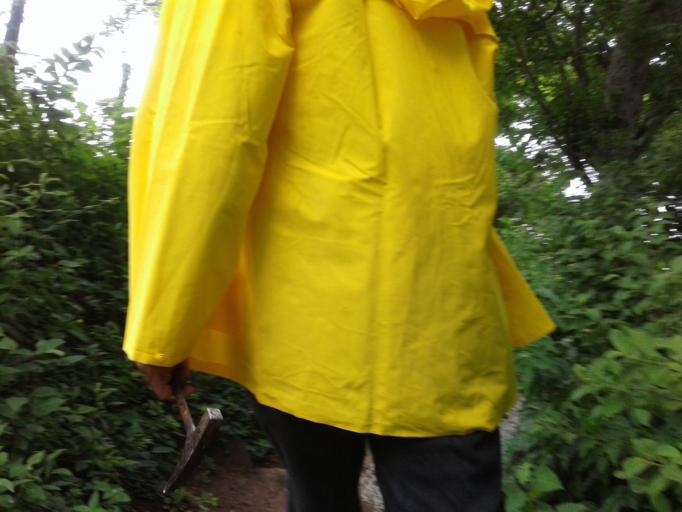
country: NI
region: Leon
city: Santa Rosa del Penon
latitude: 12.9099
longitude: -86.2207
